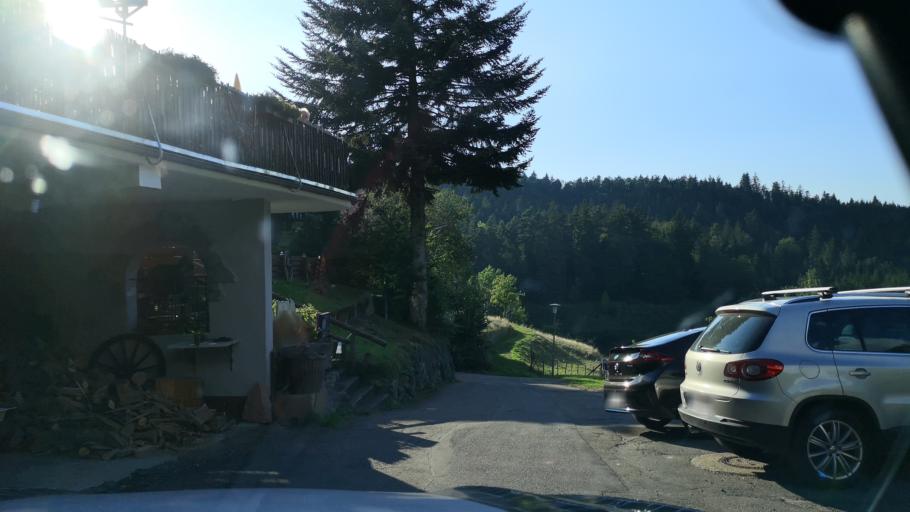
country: DE
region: Baden-Wuerttemberg
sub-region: Karlsruhe Region
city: Bad Herrenalb
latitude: 48.7685
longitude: 8.4355
